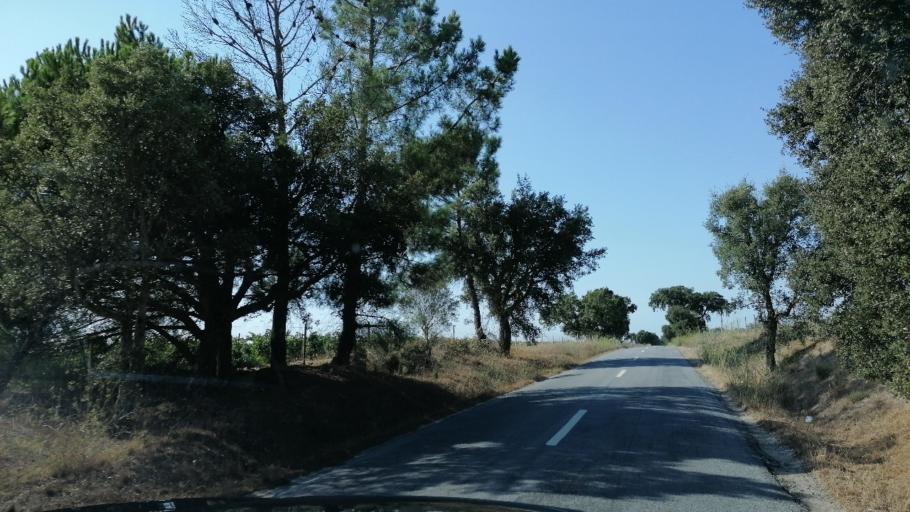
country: PT
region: Evora
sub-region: Vendas Novas
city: Vendas Novas
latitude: 38.7402
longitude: -8.6273
